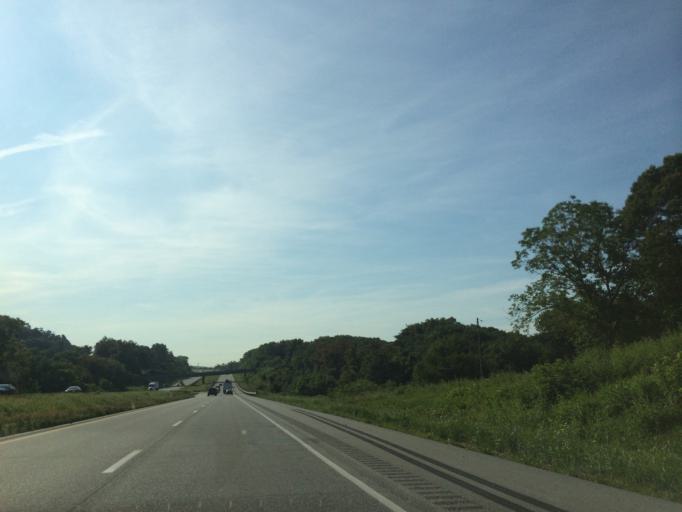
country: US
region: Pennsylvania
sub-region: Lancaster County
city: Columbia
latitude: 40.0437
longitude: -76.4862
